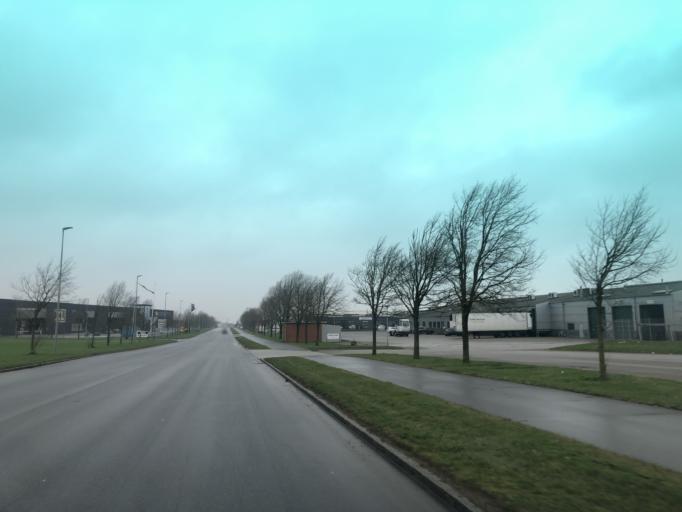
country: DK
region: Central Jutland
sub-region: Struer Kommune
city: Struer
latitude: 56.4730
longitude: 8.5832
